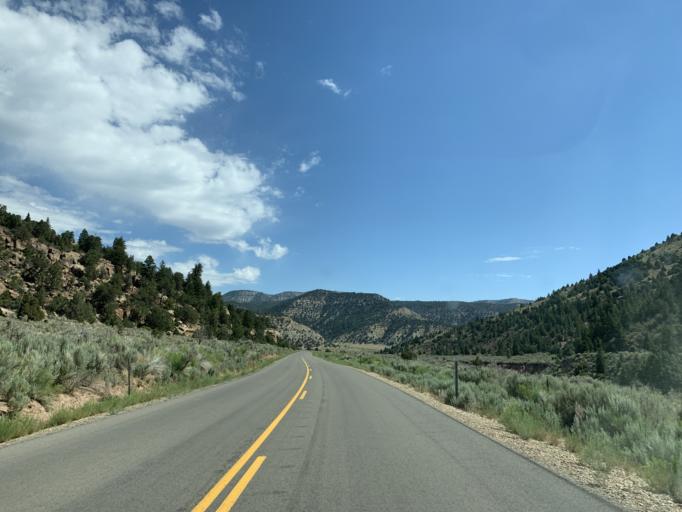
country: US
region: Utah
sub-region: Carbon County
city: East Carbon City
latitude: 39.7646
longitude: -110.5208
